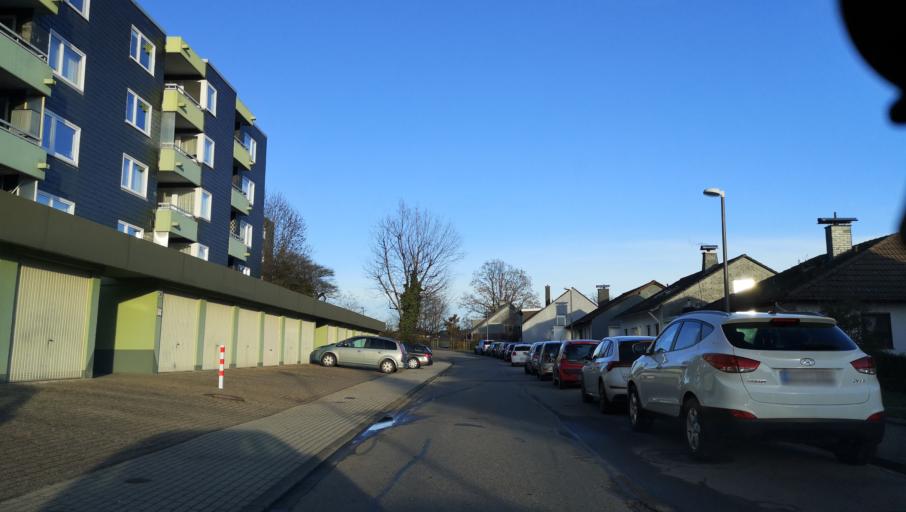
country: DE
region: North Rhine-Westphalia
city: Radevormwald
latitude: 51.2082
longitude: 7.3586
